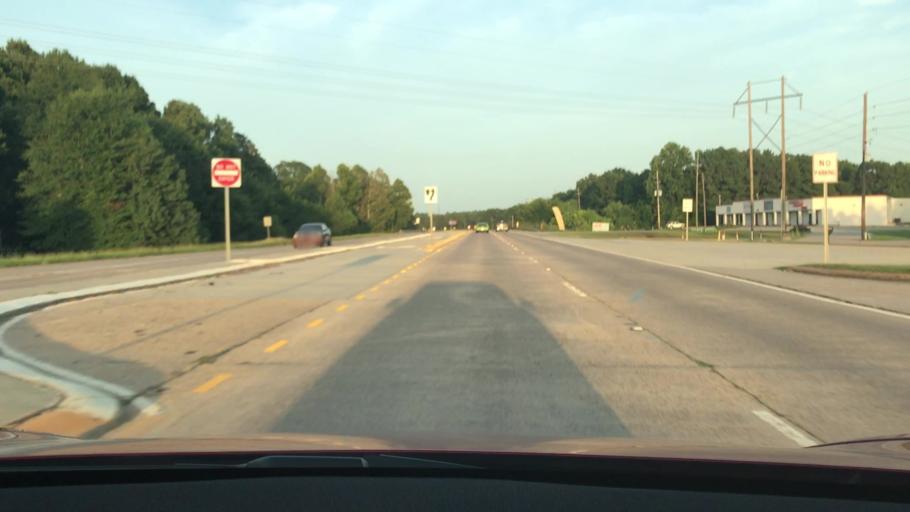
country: US
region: Louisiana
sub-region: Bossier Parish
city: Bossier City
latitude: 32.4009
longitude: -93.7746
